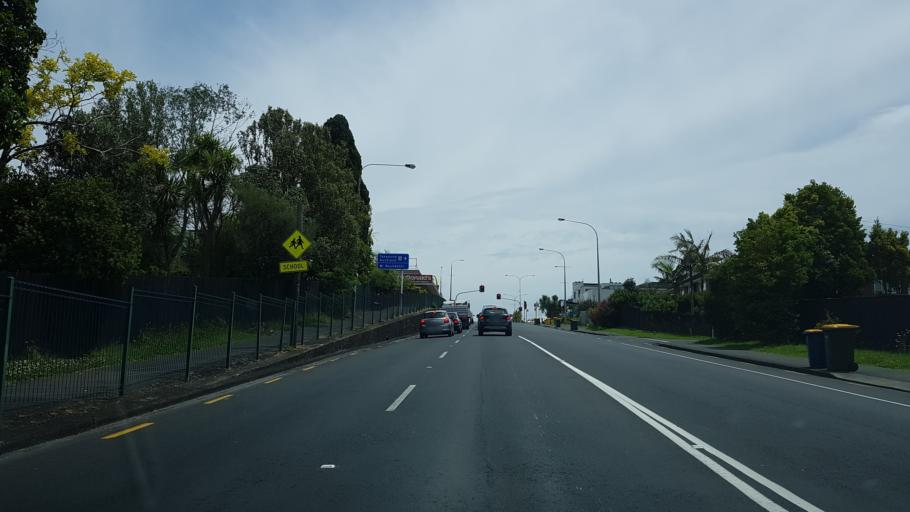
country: NZ
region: Auckland
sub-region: Auckland
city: North Shore
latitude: -36.8096
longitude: 174.7908
